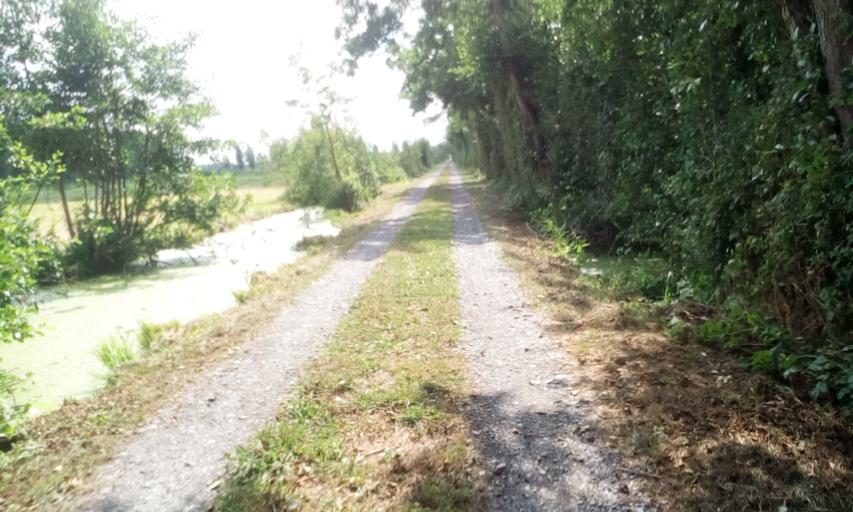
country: FR
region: Lower Normandy
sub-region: Departement du Calvados
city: Bavent
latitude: 49.2311
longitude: -0.1687
